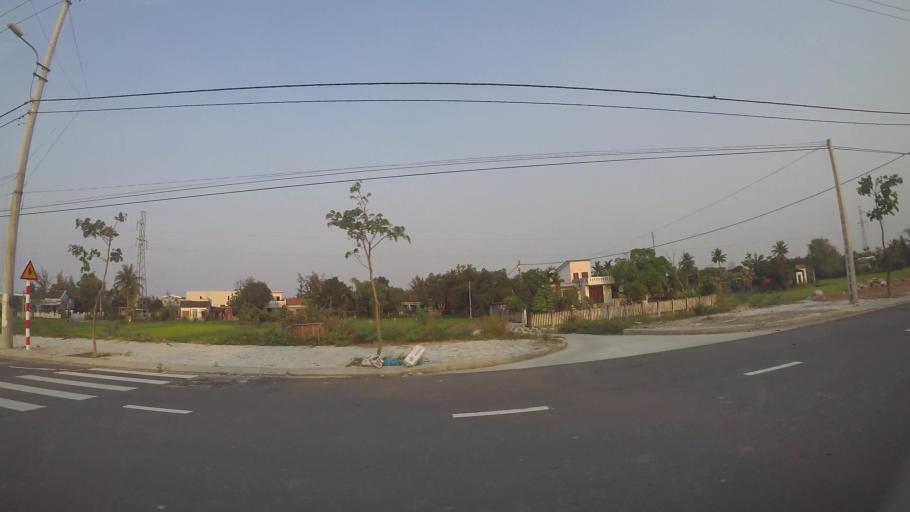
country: VN
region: Da Nang
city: Ngu Hanh Son
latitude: 15.9655
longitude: 108.2313
